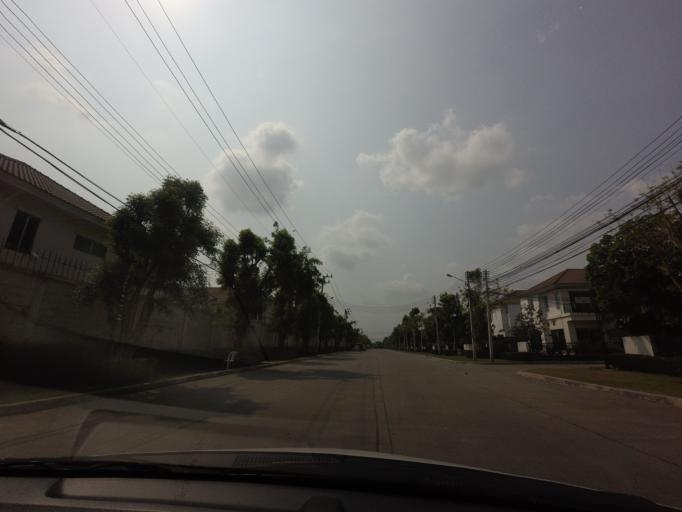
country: TH
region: Pathum Thani
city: Khlong Luang
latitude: 14.0003
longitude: 100.6602
